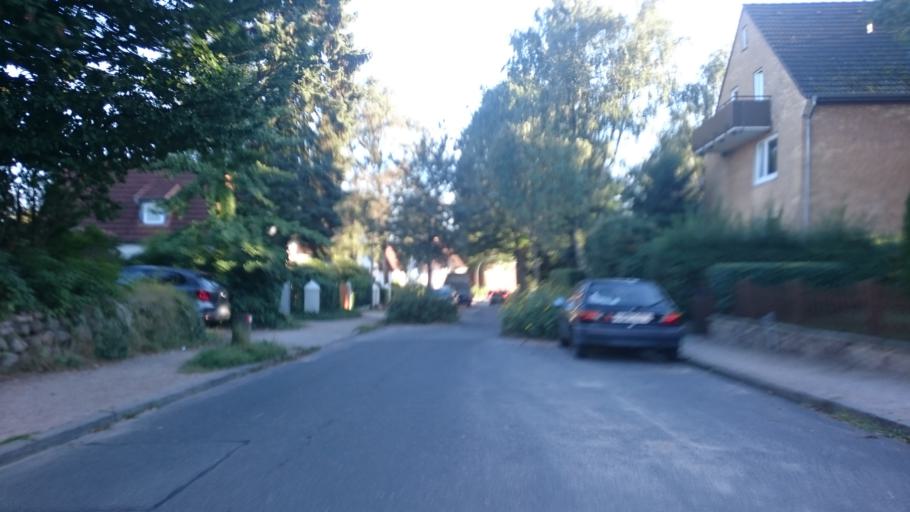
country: DE
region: Hamburg
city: Eidelstedt
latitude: 53.5707
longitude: 9.8804
